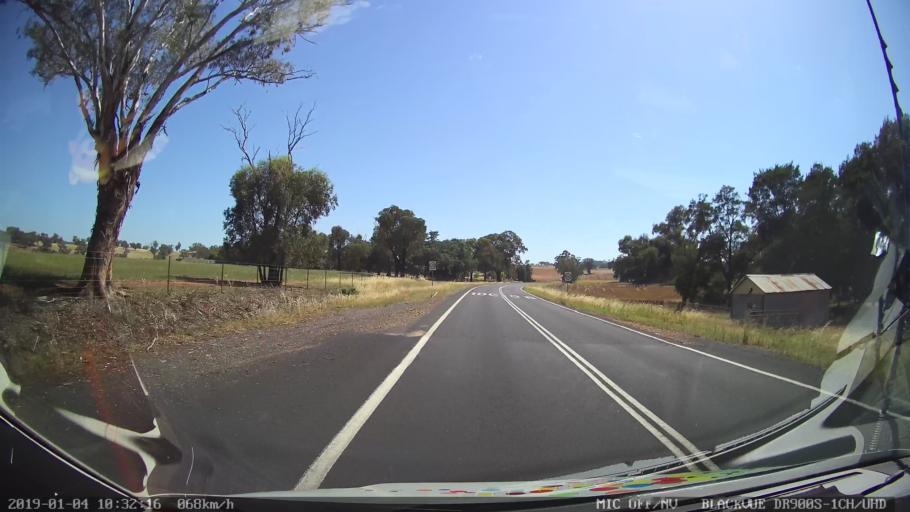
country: AU
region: New South Wales
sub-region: Cabonne
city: Canowindra
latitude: -33.3278
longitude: 148.6376
